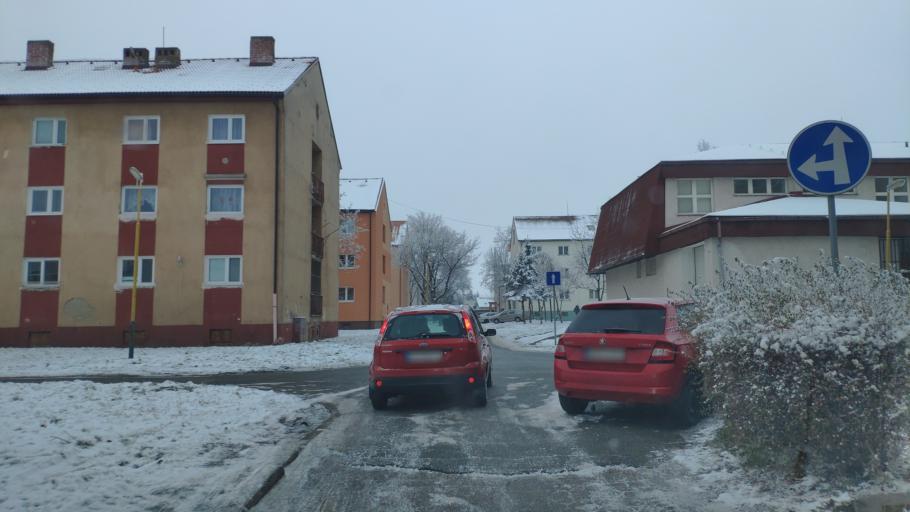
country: SK
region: Kosicky
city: Kosice
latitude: 48.6361
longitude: 21.1735
